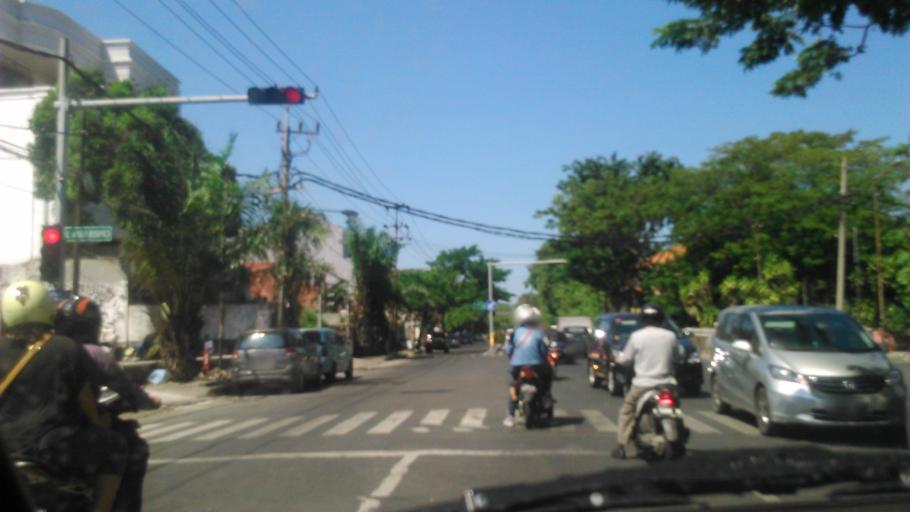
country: ID
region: East Java
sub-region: Kota Surabaya
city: Surabaya
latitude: -7.2560
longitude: 112.7484
